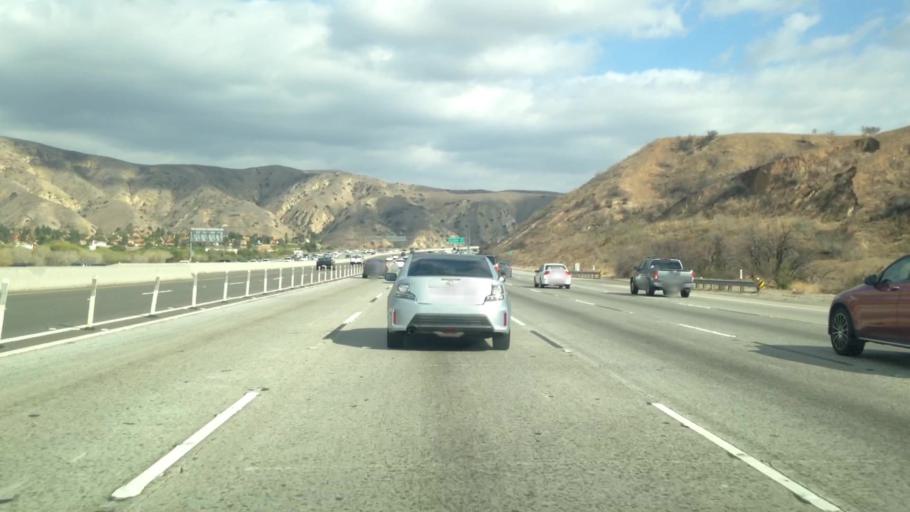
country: US
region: California
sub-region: San Bernardino County
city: Los Serranos
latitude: 33.8710
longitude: -117.7022
